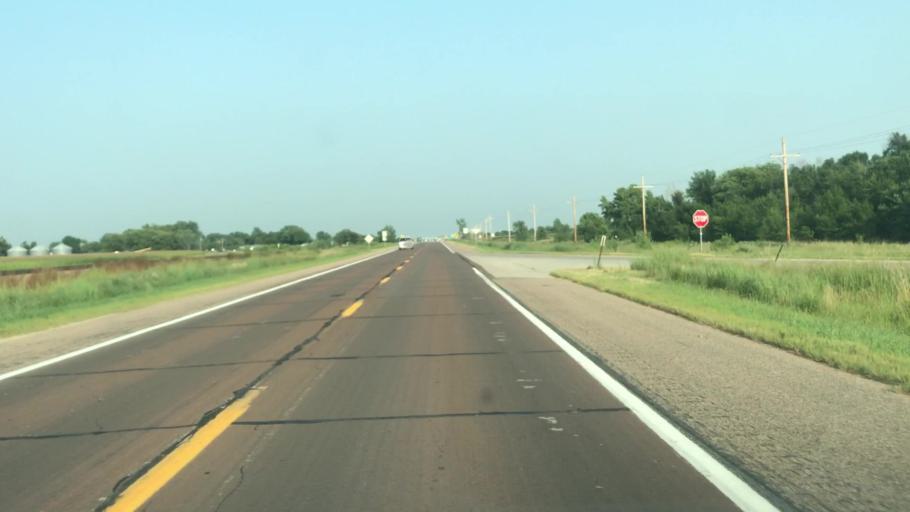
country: US
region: Nebraska
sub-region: Hall County
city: Grand Island
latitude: 40.9607
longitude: -98.4166
